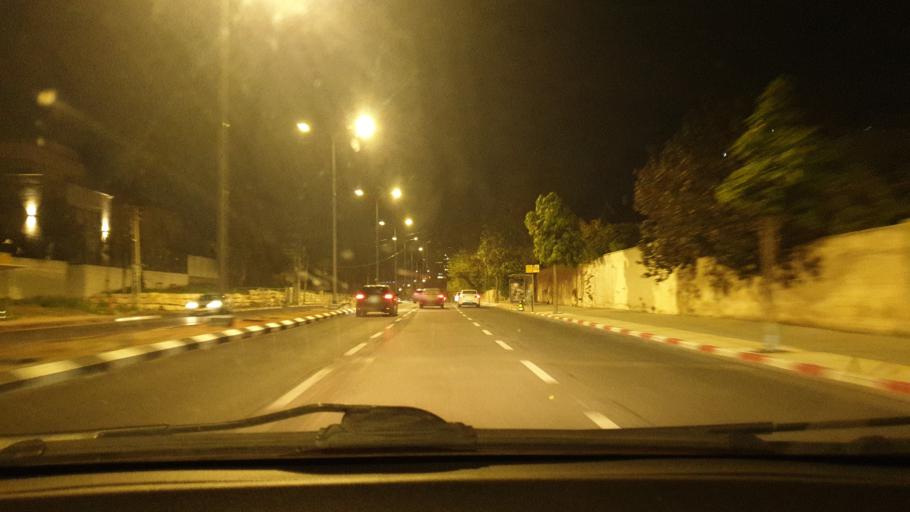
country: IL
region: Tel Aviv
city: Ramat Gan
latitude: 32.1198
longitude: 34.8083
